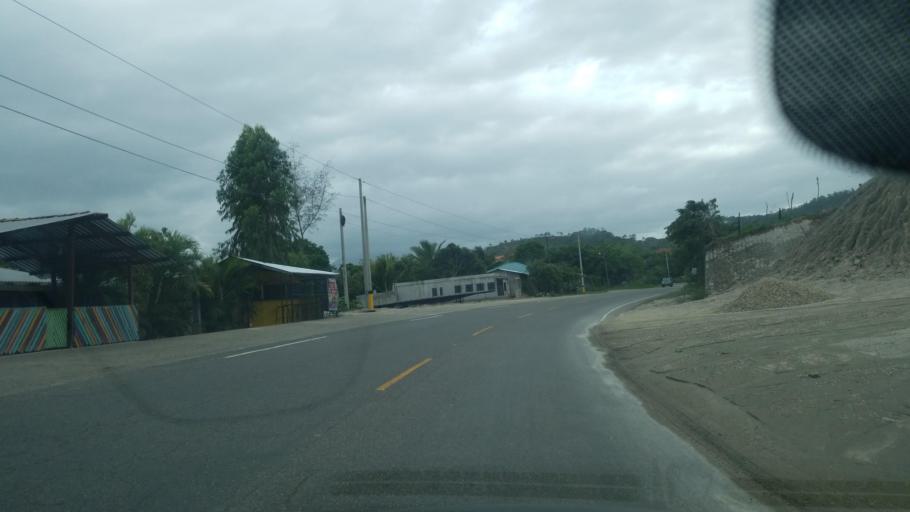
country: HN
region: Ocotepeque
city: Lucerna
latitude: 14.5604
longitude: -88.9360
